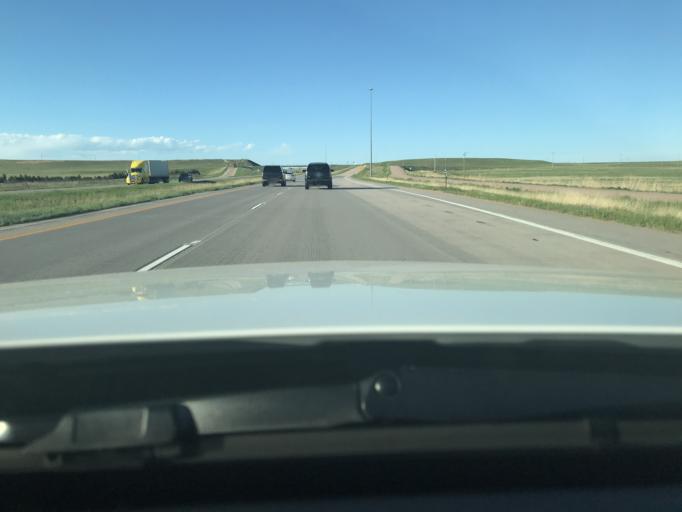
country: US
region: Colorado
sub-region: Larimer County
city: Wellington
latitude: 40.9062
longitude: -104.9412
